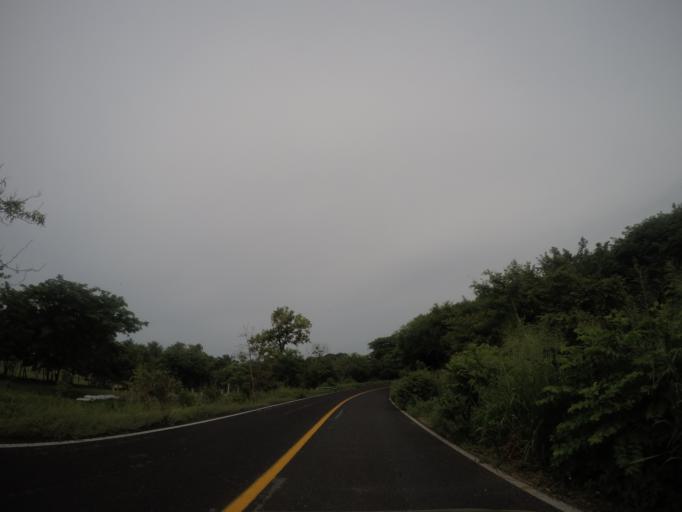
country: MX
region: Oaxaca
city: San Pedro Mixtepec
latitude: 15.9498
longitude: -97.2673
